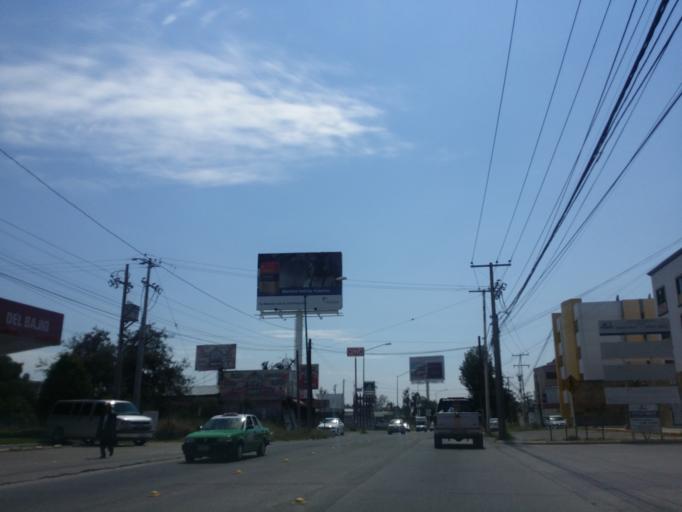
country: MX
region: Guanajuato
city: Leon
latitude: 21.1618
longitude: -101.6837
